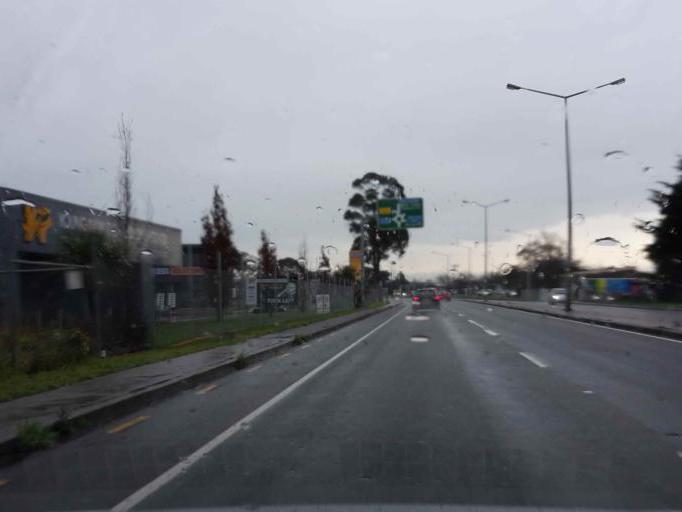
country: NZ
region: Canterbury
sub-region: Selwyn District
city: Prebbleton
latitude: -43.5392
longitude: 172.5573
